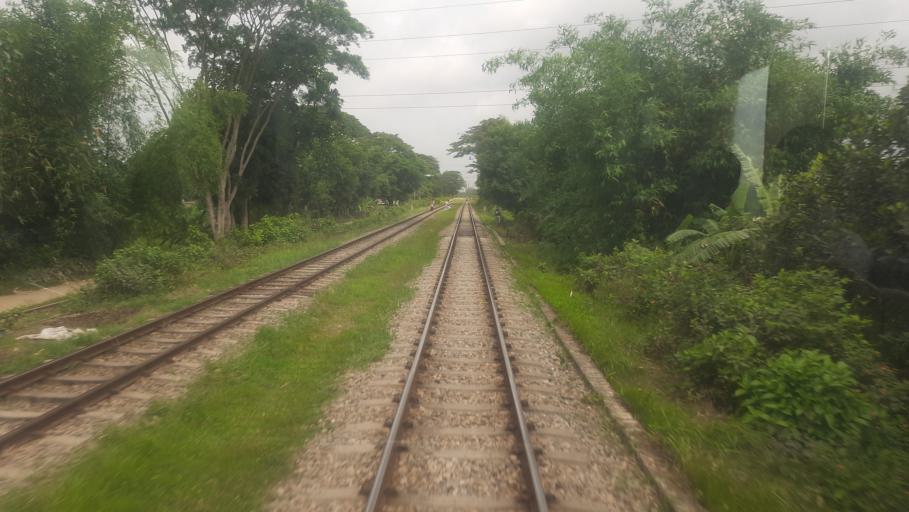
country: BD
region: Dhaka
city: Bhairab Bazar
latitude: 24.0303
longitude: 91.0121
